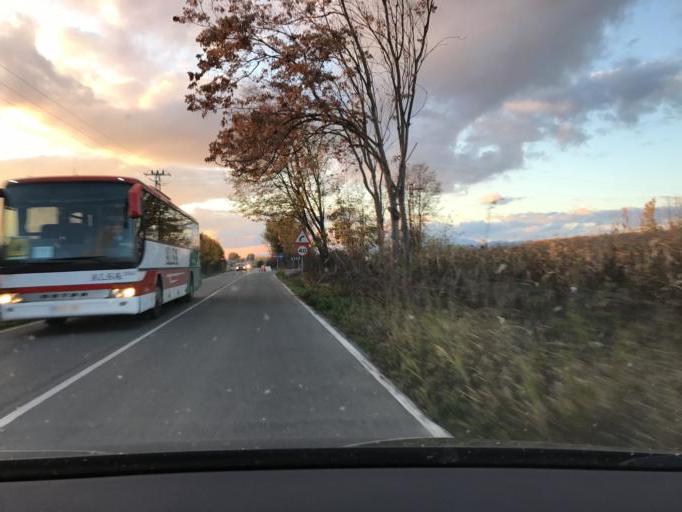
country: ES
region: Andalusia
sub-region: Provincia de Granada
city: Atarfe
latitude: 37.1919
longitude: -3.6849
